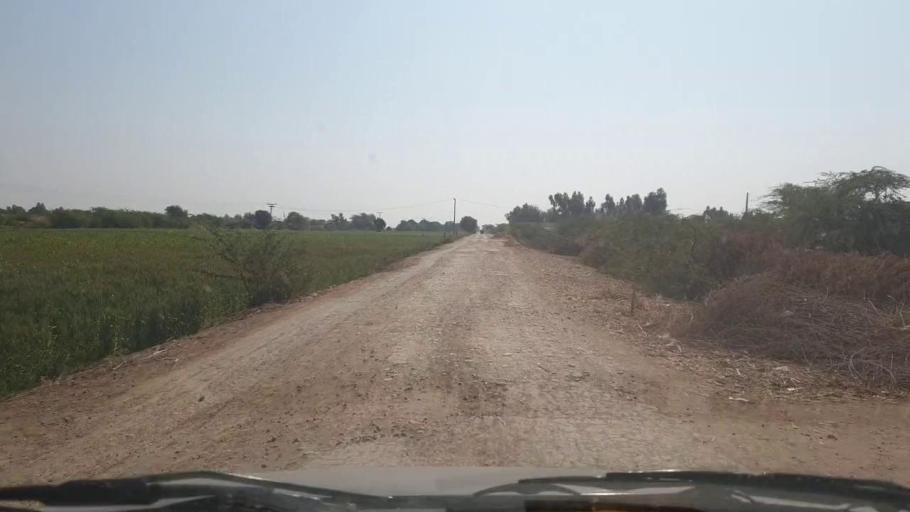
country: PK
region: Sindh
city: Samaro
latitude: 25.2729
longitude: 69.3441
